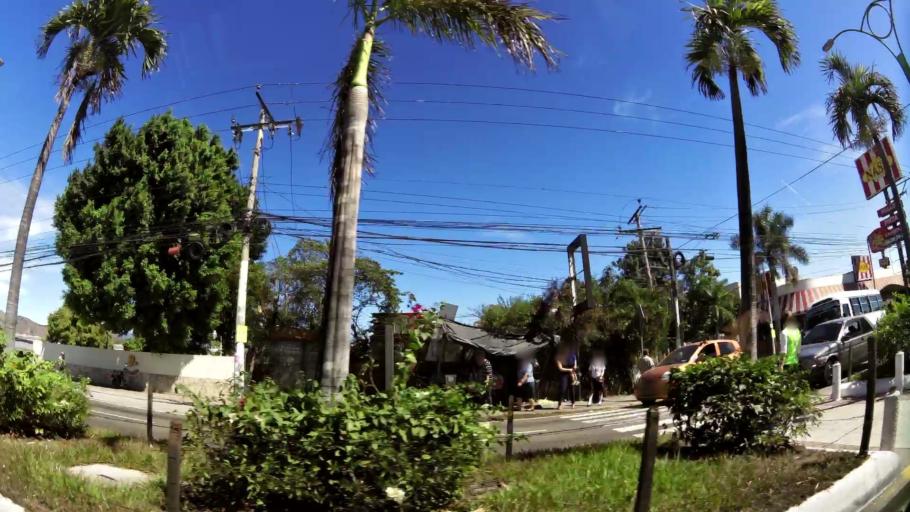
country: SV
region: San Salvador
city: Apopa
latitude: 13.7923
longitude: -89.1760
